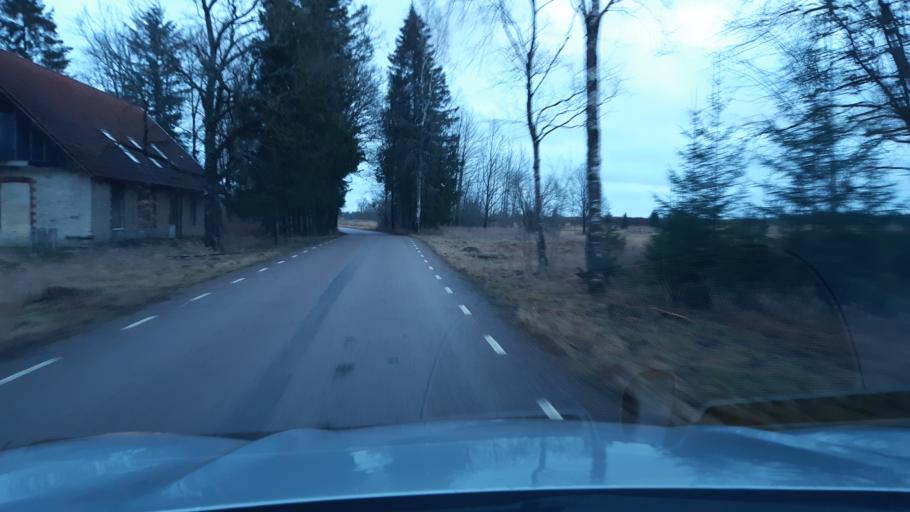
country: EE
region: Raplamaa
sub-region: Rapla vald
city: Rapla
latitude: 58.9970
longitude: 24.7186
